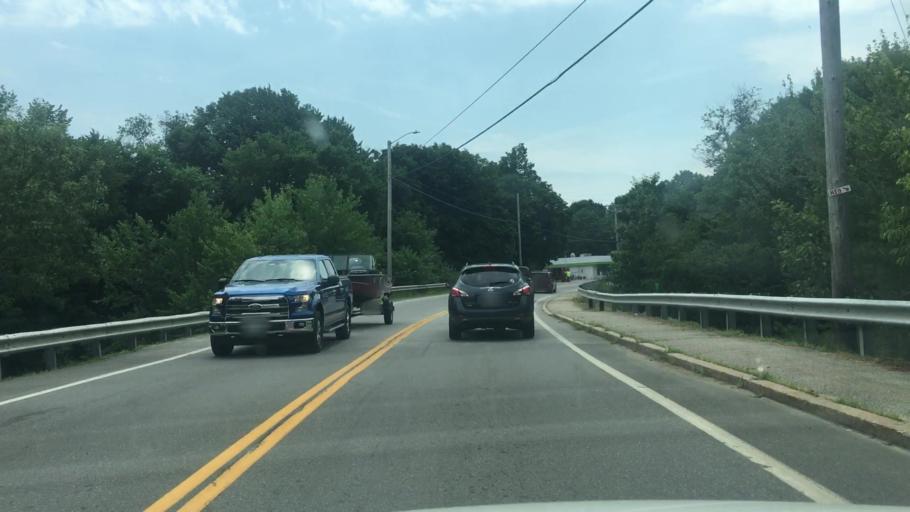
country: US
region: New Hampshire
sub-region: Strafford County
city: Rochester
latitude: 43.3357
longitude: -70.9402
